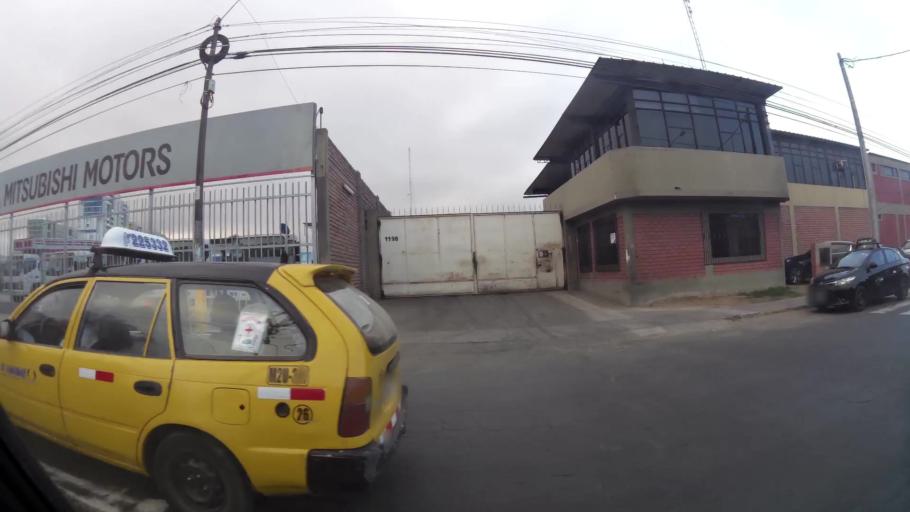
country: PE
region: La Libertad
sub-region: Provincia de Trujillo
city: La Esperanza
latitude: -8.0935
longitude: -79.0339
